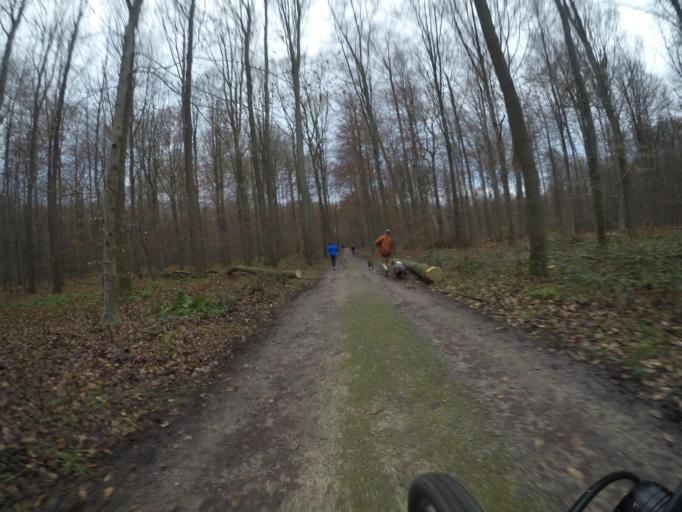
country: BE
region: Flanders
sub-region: Provincie Vlaams-Brabant
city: Hoeilaart
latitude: 50.7566
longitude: 4.4438
